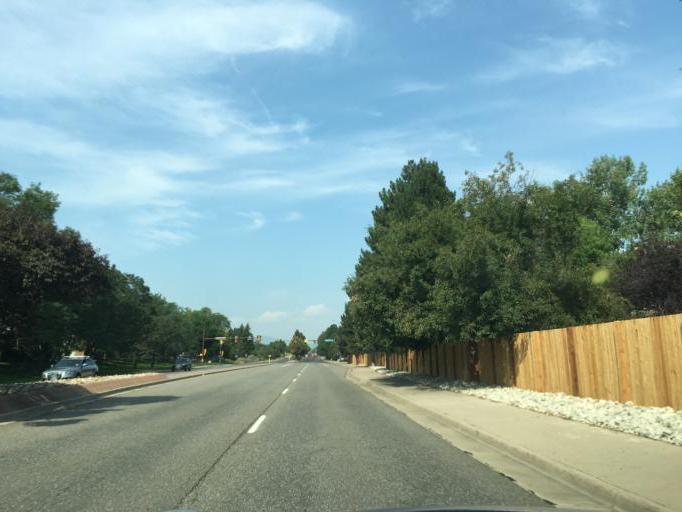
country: US
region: Colorado
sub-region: Jefferson County
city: Arvada
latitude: 39.8419
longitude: -105.0972
